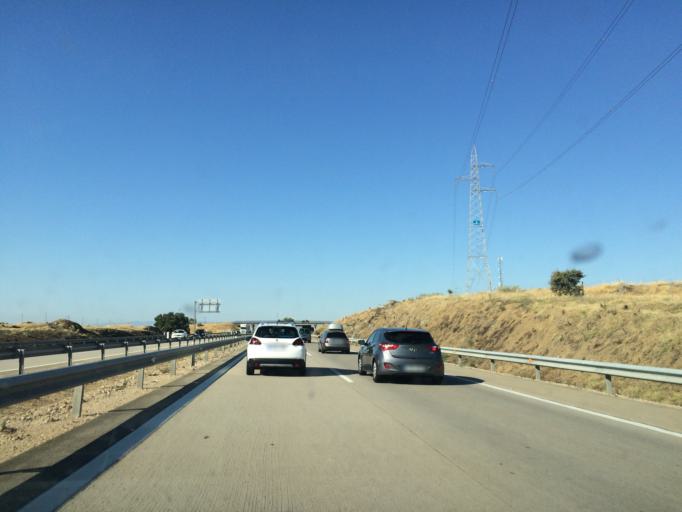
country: ES
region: Castille-La Mancha
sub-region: Province of Toledo
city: Talavera de la Reina
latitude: 39.9806
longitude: -4.8529
